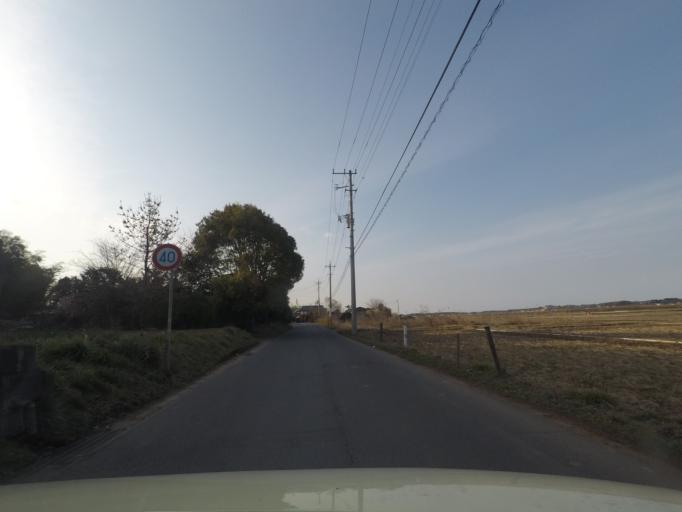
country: JP
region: Ibaraki
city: Okunoya
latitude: 36.2685
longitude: 140.4437
